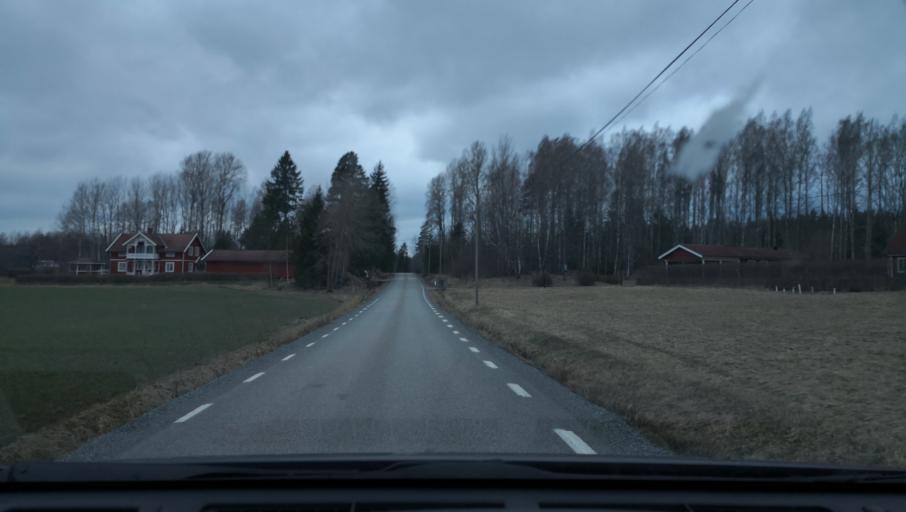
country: SE
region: Vaestmanland
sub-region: Kopings Kommun
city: Kolsva
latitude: 59.5628
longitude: 15.7380
